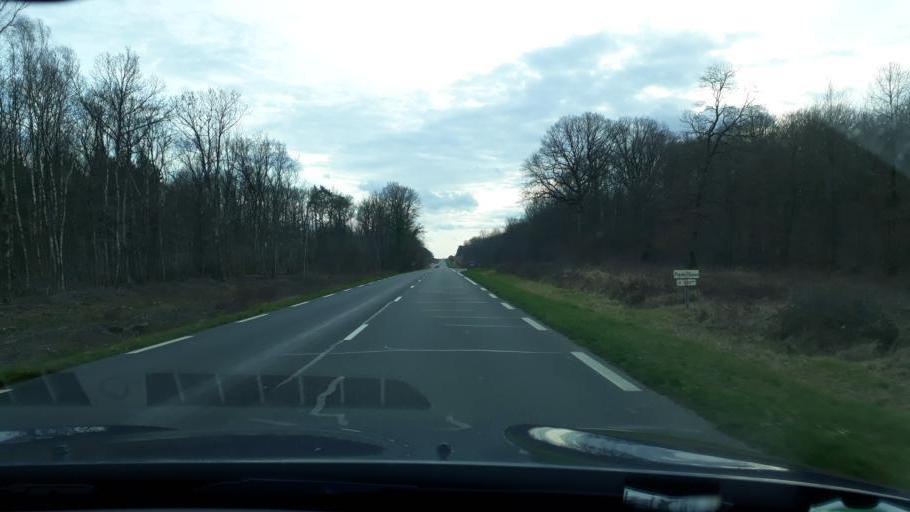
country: FR
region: Centre
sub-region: Departement du Loiret
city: Chilleurs-aux-Bois
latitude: 48.0416
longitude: 2.1232
